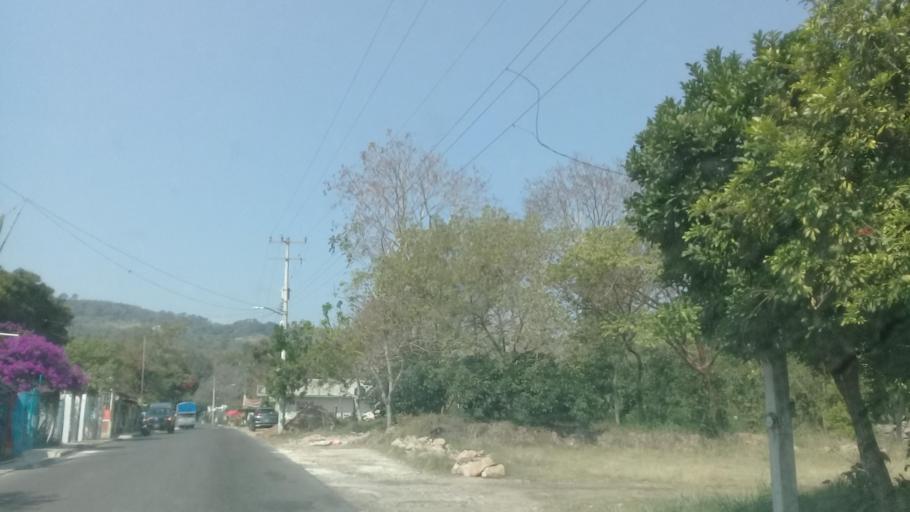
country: MX
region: Veracruz
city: El Castillo
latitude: 19.5723
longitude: -96.8339
